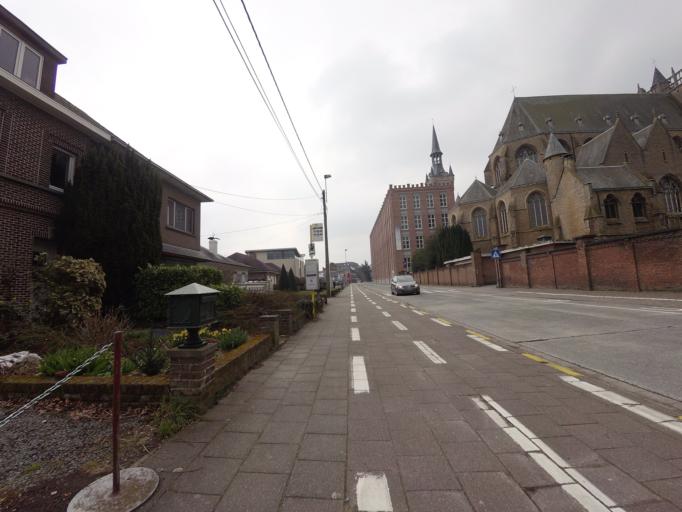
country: BE
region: Flanders
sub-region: Provincie Antwerpen
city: Sint-Katelijne-Waver
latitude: 51.0657
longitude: 4.5784
